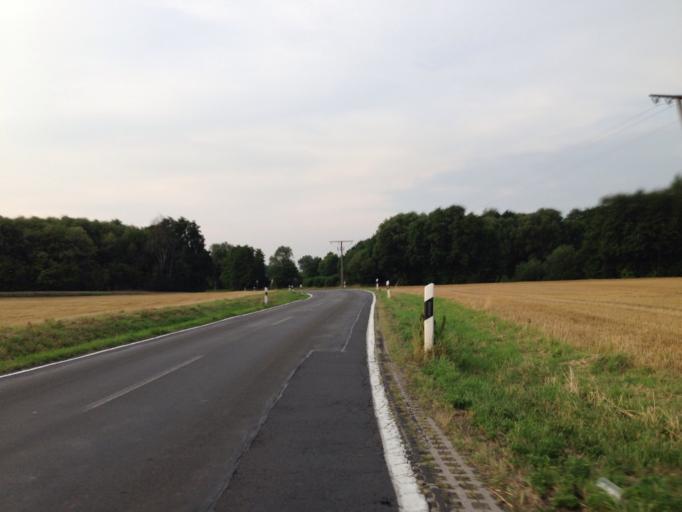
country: DE
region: Hesse
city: Allendorf an der Lahn
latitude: 50.5531
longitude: 8.6146
